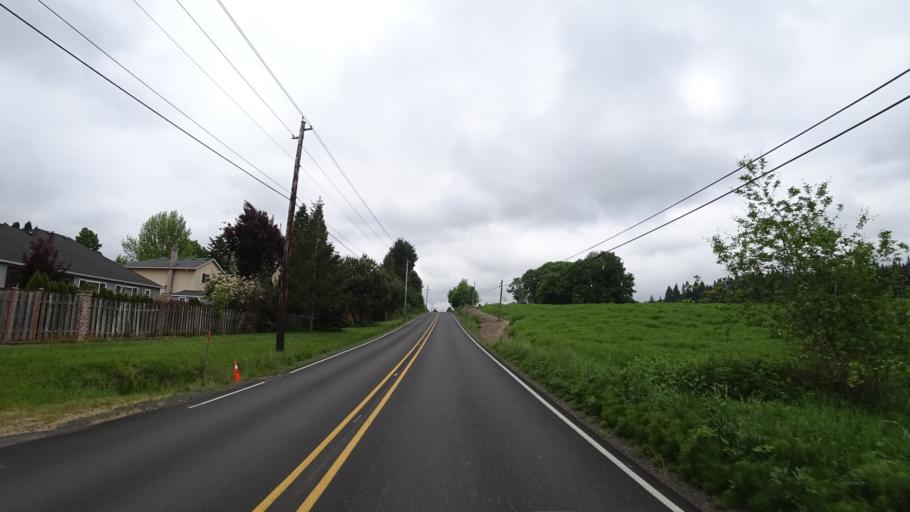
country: US
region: Oregon
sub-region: Washington County
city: Rockcreek
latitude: 45.5625
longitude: -122.8872
